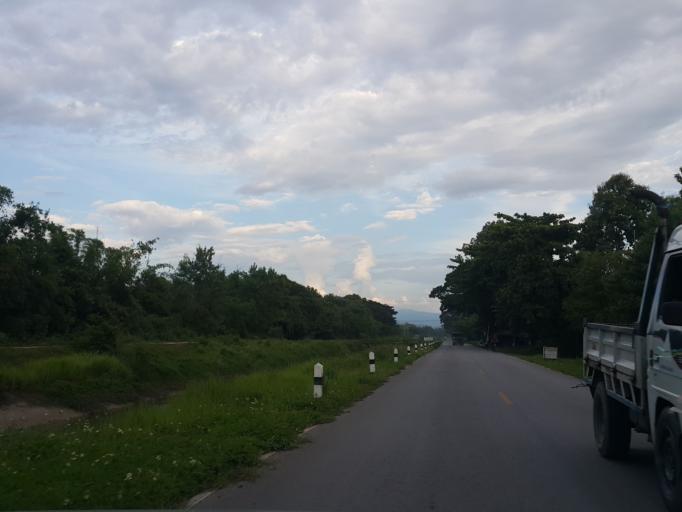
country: TH
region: Chiang Mai
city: San Sai
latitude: 18.8936
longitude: 99.0657
